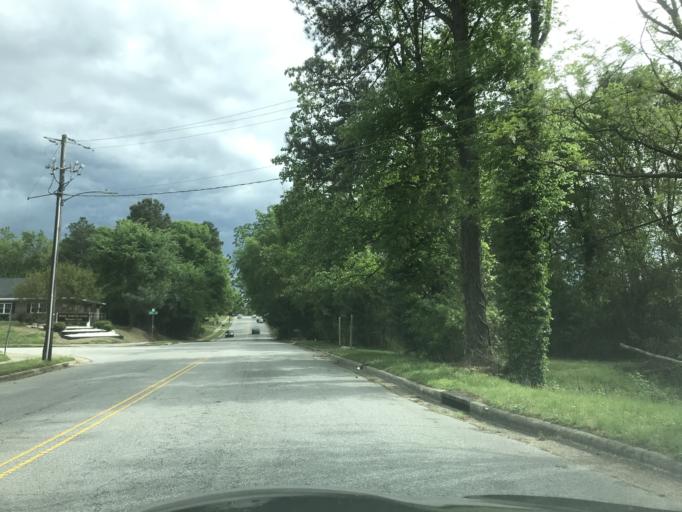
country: US
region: North Carolina
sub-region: Wake County
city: Raleigh
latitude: 35.7788
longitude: -78.5918
